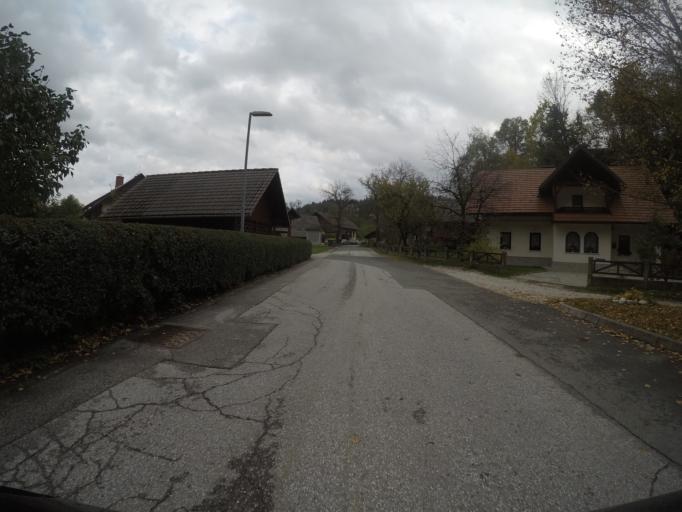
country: SI
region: Gorje
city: Zgornje Gorje
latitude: 46.3782
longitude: 14.0545
